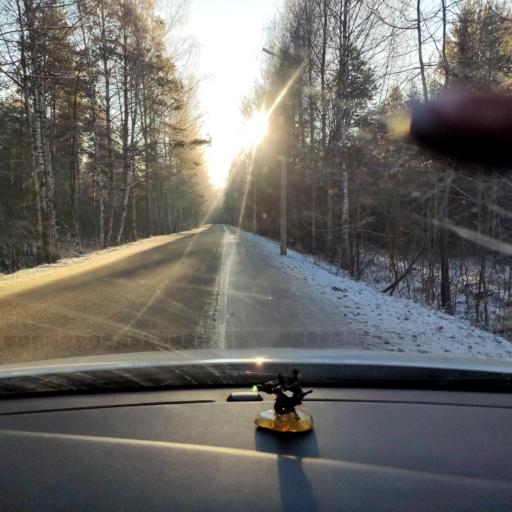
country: RU
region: Tatarstan
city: Stolbishchi
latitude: 55.6738
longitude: 49.1190
